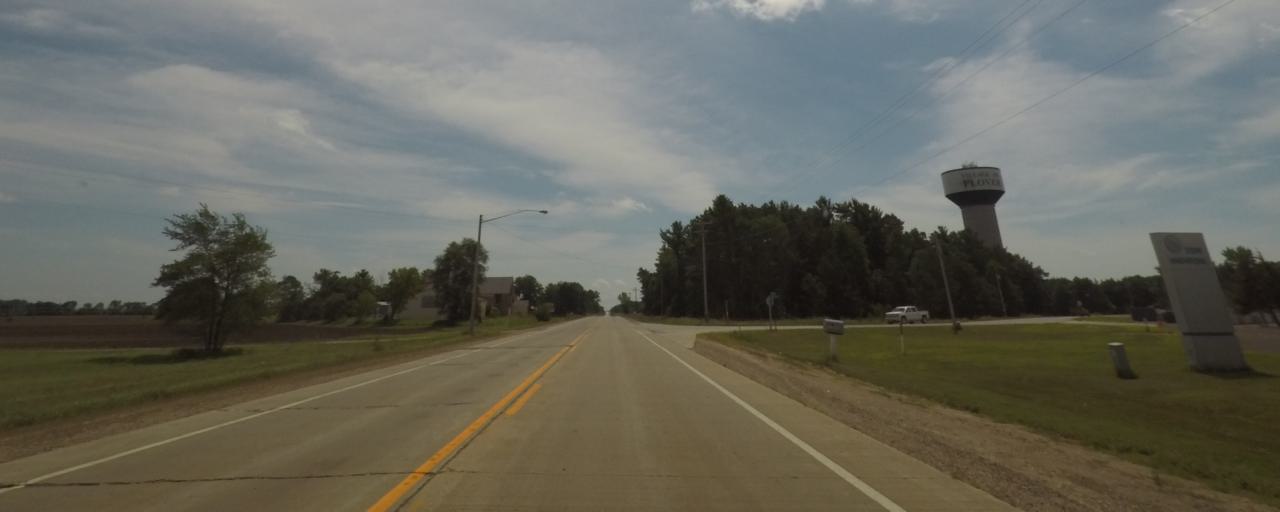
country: US
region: Wisconsin
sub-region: Portage County
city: Plover
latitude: 44.4450
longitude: -89.5394
